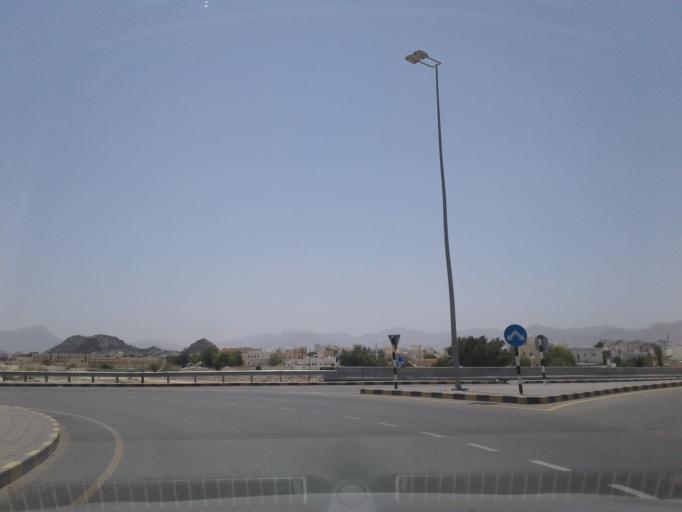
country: OM
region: Muhafazat Masqat
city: Bawshar
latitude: 23.4798
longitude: 58.4973
